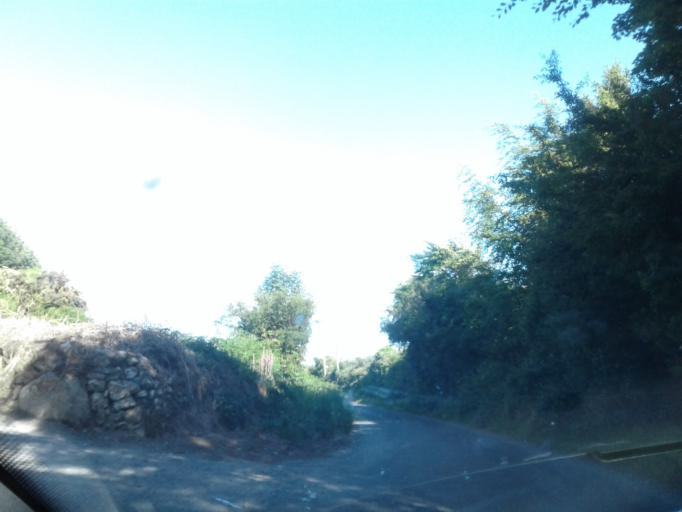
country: IE
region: Leinster
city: Ballinteer
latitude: 53.1908
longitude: -6.2603
